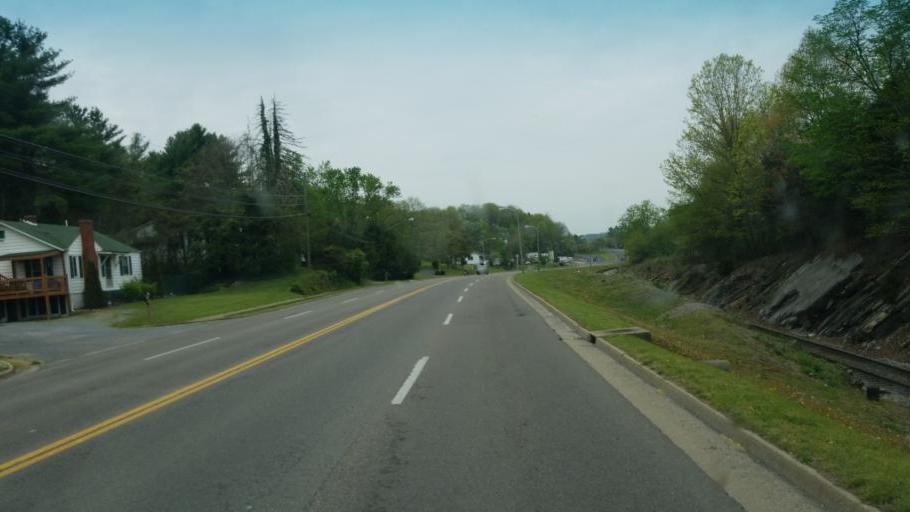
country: US
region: Virginia
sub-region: Smyth County
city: Marion
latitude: 36.8256
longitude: -81.5338
